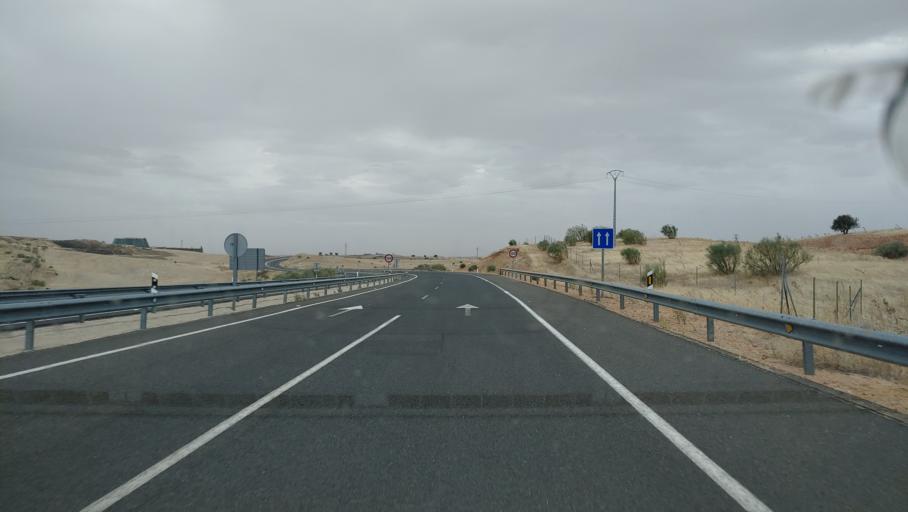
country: ES
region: Castille-La Mancha
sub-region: Provincia de Ciudad Real
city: Canada de Calatrava
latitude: 38.8741
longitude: -4.0059
